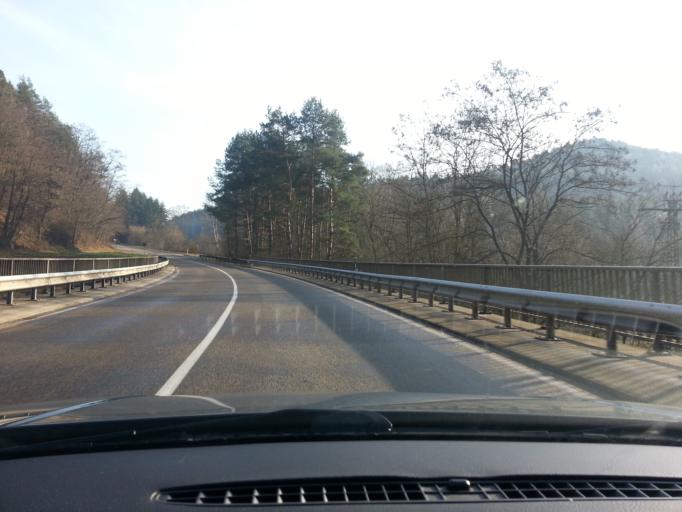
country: DE
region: Rheinland-Pfalz
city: Lug
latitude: 49.1790
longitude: 7.8973
